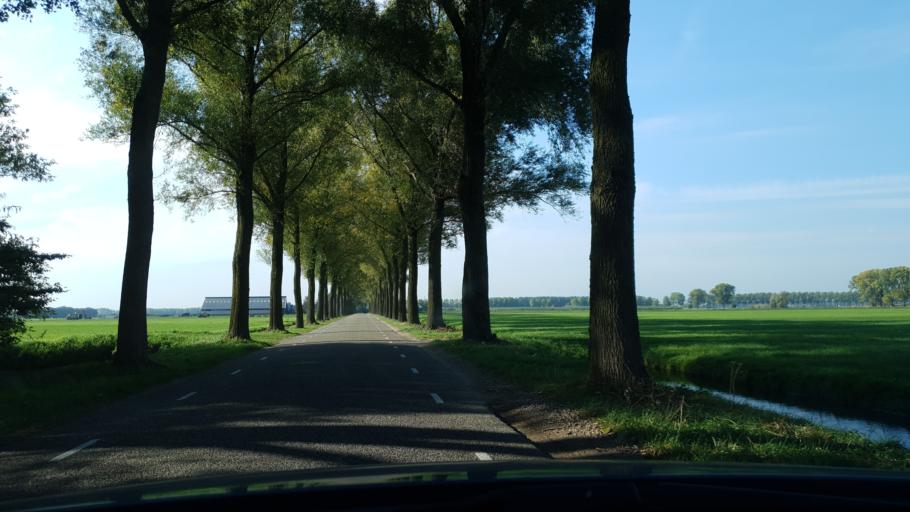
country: NL
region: Gelderland
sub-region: Gemeente Wijchen
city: Wijchen
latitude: 51.8419
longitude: 5.7252
